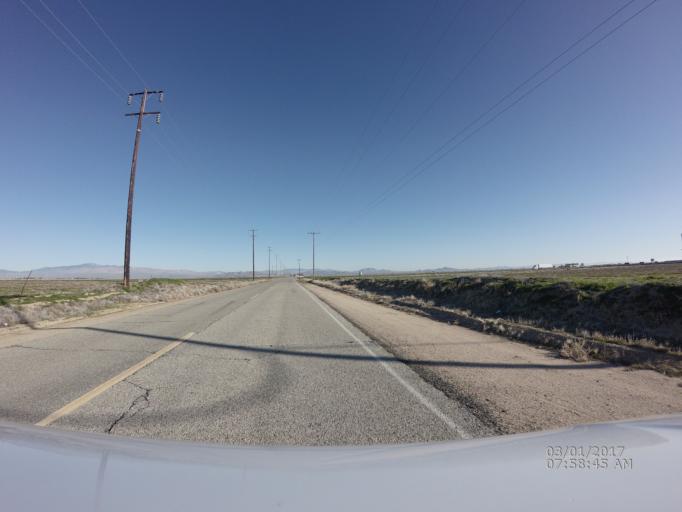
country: US
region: California
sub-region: Kern County
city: Rosamond
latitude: 34.7749
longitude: -118.2549
